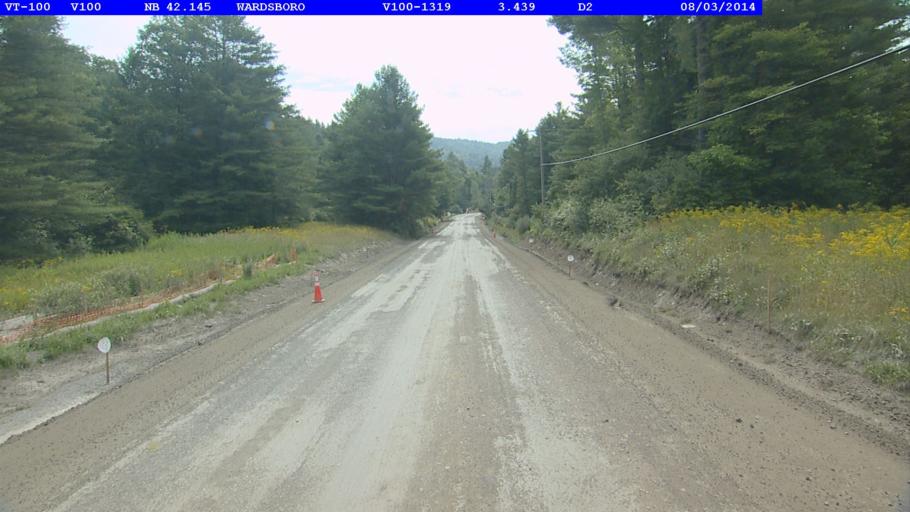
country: US
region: Vermont
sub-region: Windham County
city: Dover
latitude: 43.0290
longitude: -72.8340
